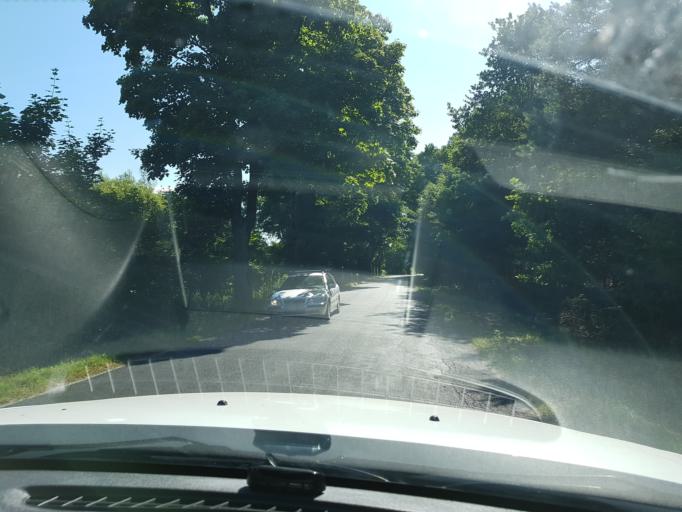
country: PL
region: West Pomeranian Voivodeship
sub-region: Powiat bialogardzki
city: Bialogard
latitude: 53.9909
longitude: 15.9501
